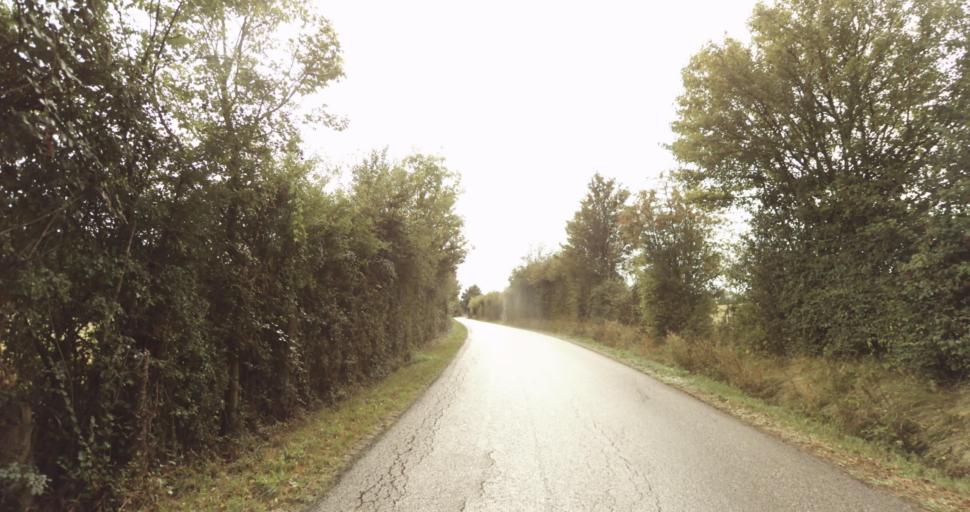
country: FR
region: Lower Normandy
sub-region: Departement de l'Orne
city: Vimoutiers
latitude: 48.8519
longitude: 0.2109
